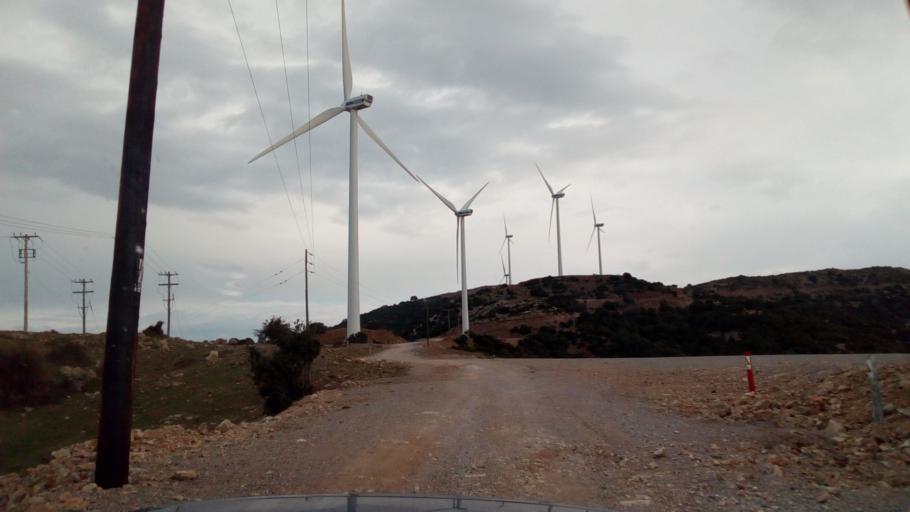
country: GR
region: West Greece
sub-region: Nomos Achaias
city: Kamarai
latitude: 38.4219
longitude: 22.0392
